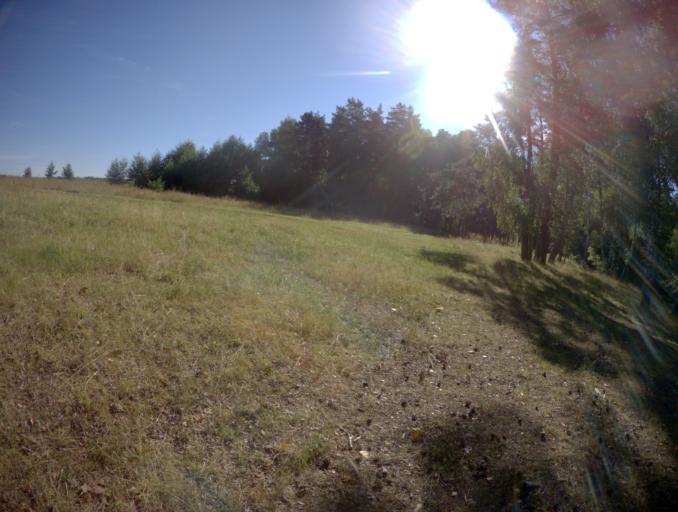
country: RU
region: Vladimir
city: Nikologory
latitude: 56.1721
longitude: 41.9440
